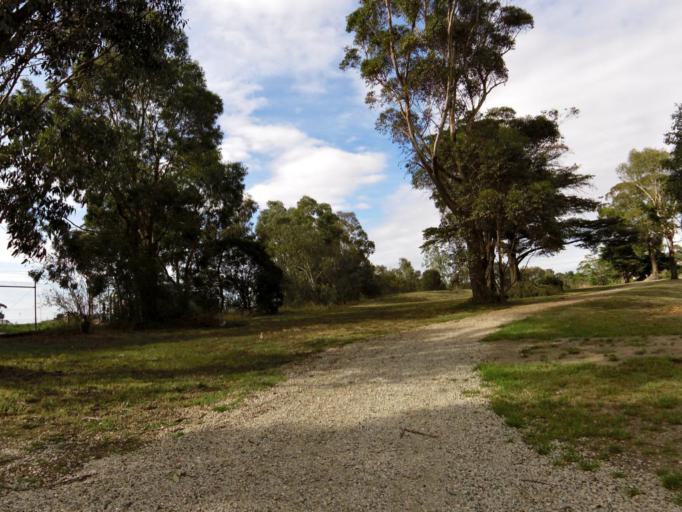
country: AU
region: Victoria
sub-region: Moreland
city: Glenroy
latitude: -37.6901
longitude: 144.9382
